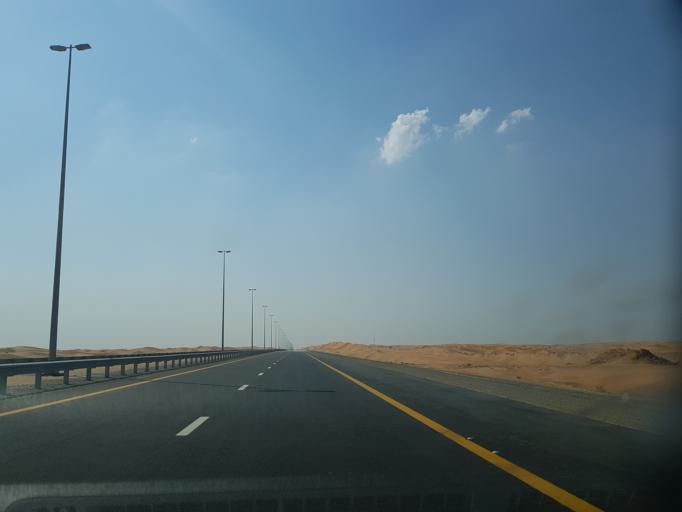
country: AE
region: Ash Shariqah
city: Adh Dhayd
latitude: 25.2567
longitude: 55.7225
